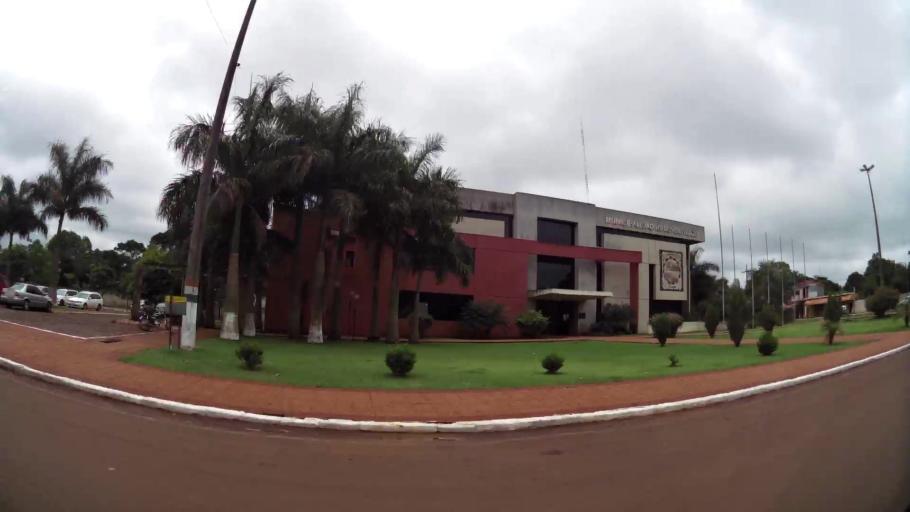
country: PY
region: Alto Parana
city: Ciudad del Este
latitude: -25.4854
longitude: -54.7642
